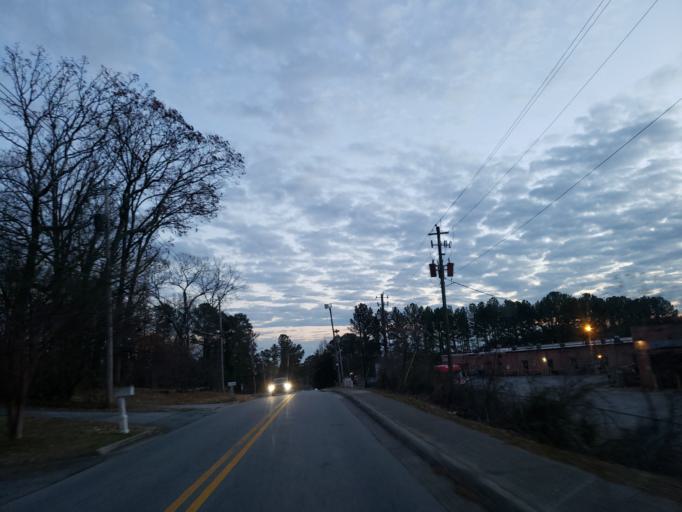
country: US
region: Georgia
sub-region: Cobb County
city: Smyrna
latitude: 33.8621
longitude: -84.5169
